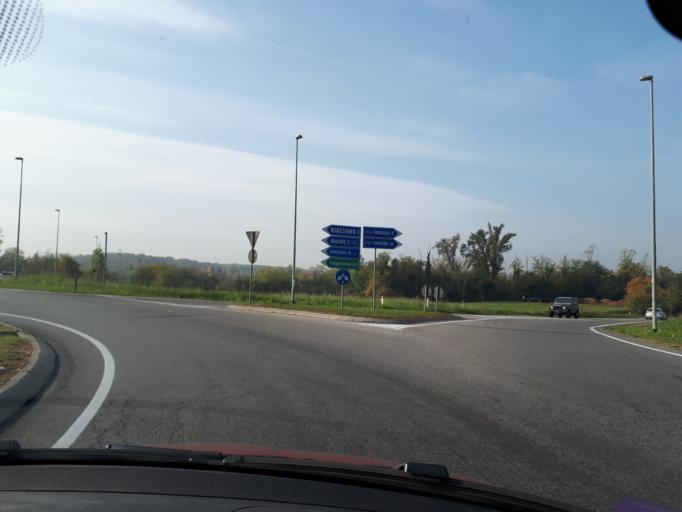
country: IT
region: Lombardy
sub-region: Provincia di Monza e Brianza
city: Lesmo
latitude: 45.6382
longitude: 9.3000
